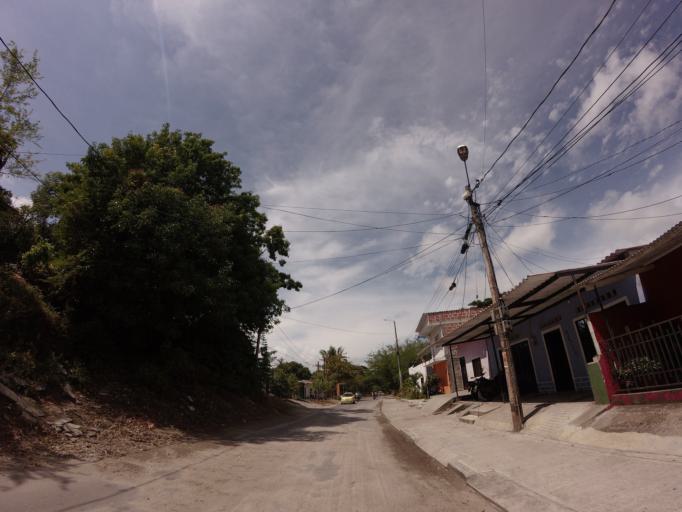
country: CO
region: Cundinamarca
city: Puerto Salgar
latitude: 5.4700
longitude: -74.6682
